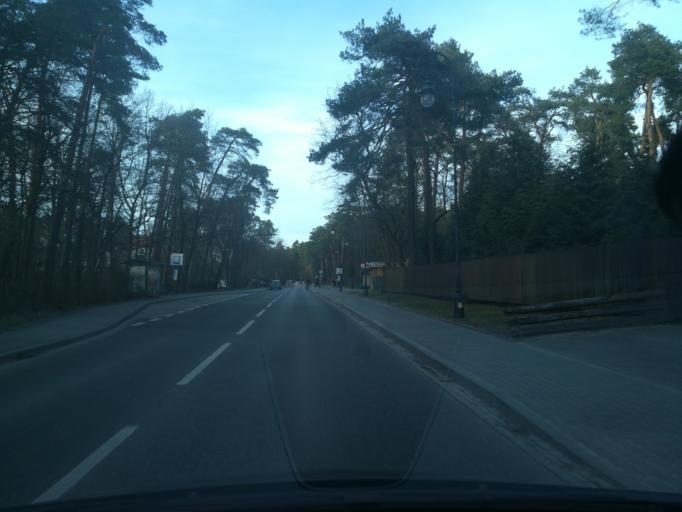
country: PL
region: Masovian Voivodeship
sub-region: Powiat piaseczynski
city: Konstancin-Jeziorna
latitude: 52.0781
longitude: 21.1180
